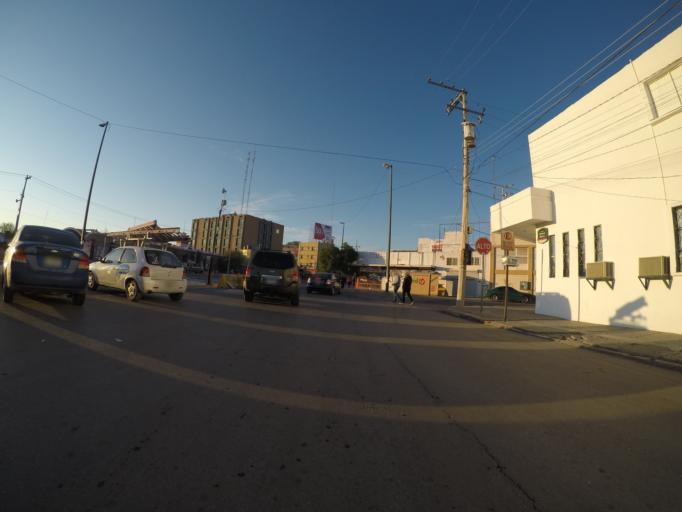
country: MX
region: Chihuahua
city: Ciudad Juarez
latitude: 31.7381
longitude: -106.4825
